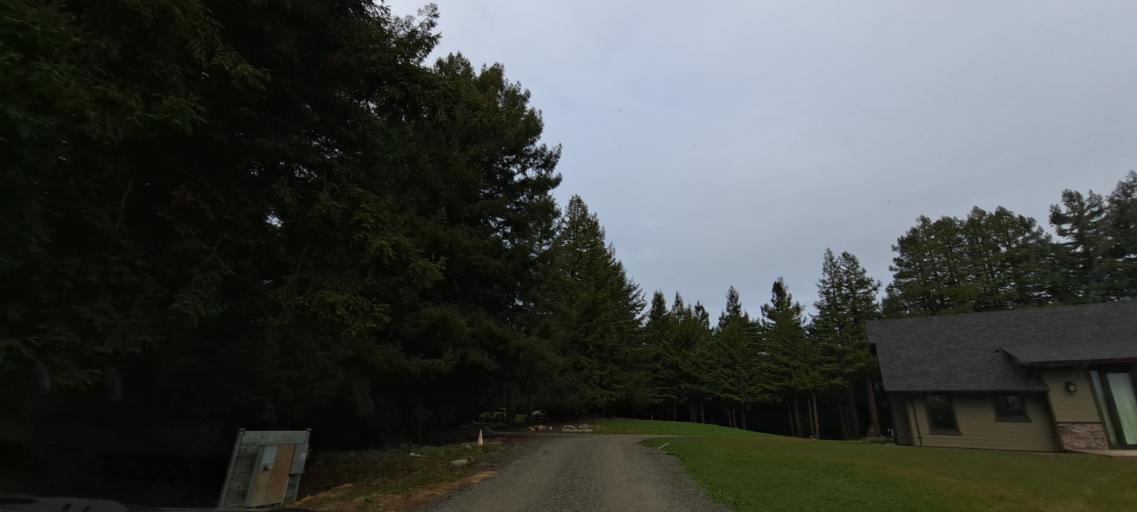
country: US
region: California
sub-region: Humboldt County
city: Fortuna
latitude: 40.6079
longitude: -124.1539
